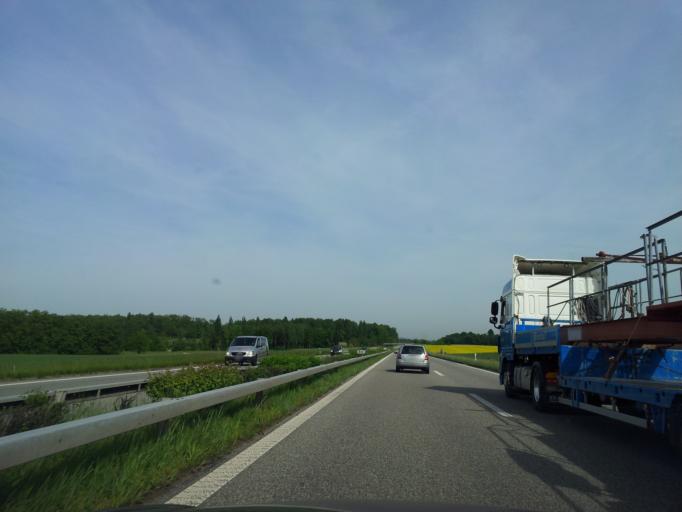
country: CH
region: Zurich
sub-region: Bezirk Buelach
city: Bachenbulach
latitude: 47.4828
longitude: 8.5479
